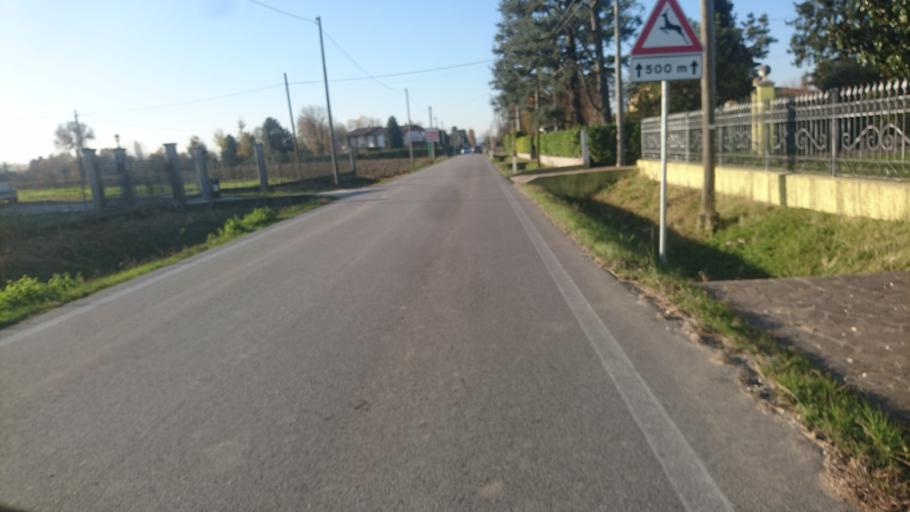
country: IT
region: Veneto
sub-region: Provincia di Padova
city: Mestrino
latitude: 45.4232
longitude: 11.7645
